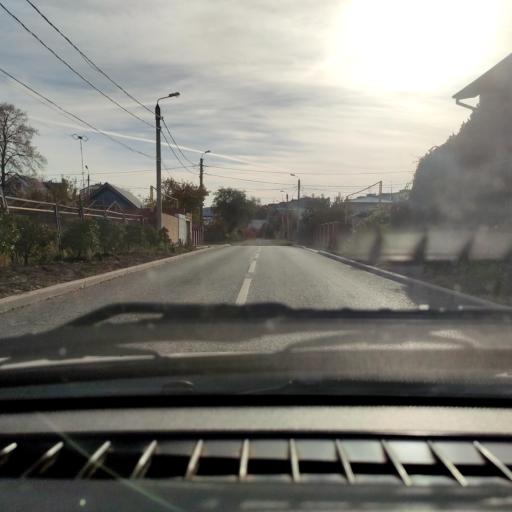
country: RU
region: Samara
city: Tol'yatti
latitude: 53.5259
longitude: 49.4163
